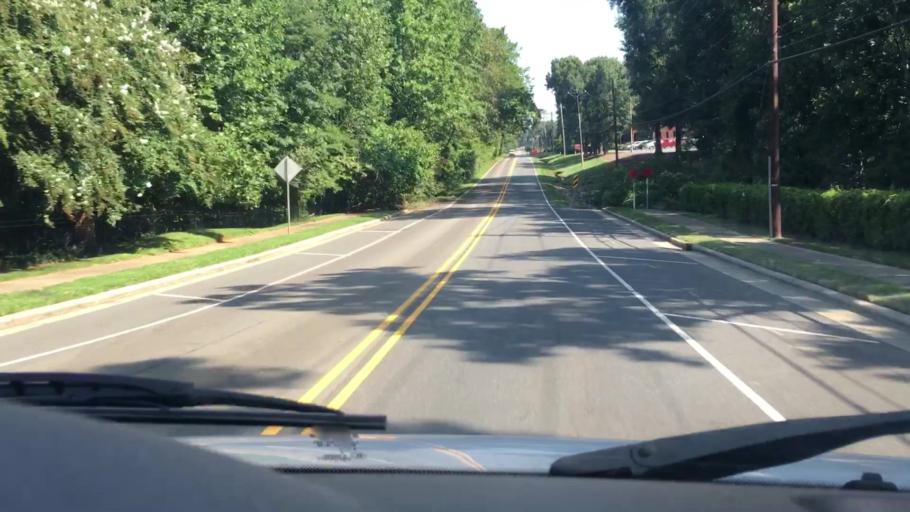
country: US
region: North Carolina
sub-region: Mecklenburg County
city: Charlotte
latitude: 35.3181
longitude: -80.8525
